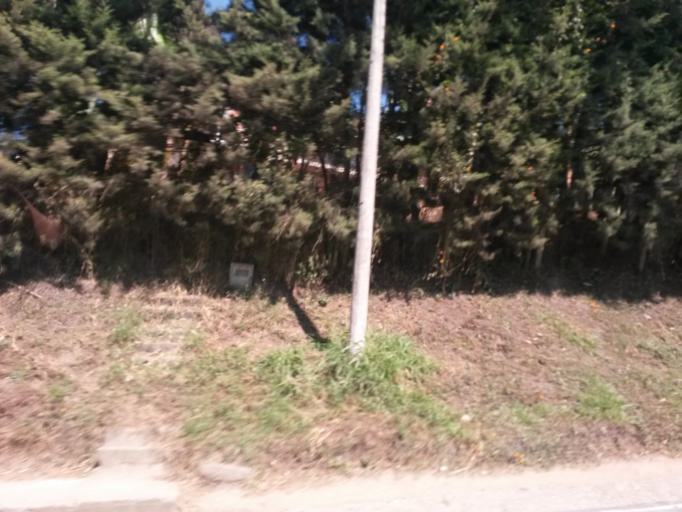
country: CO
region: Cauca
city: Popayan
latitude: 2.4571
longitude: -76.6432
